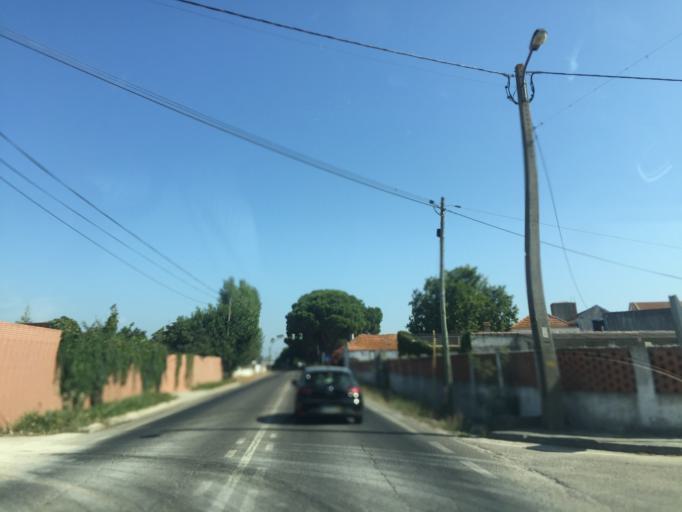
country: PT
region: Santarem
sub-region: Almeirim
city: Almeirim
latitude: 39.2290
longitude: -8.6055
